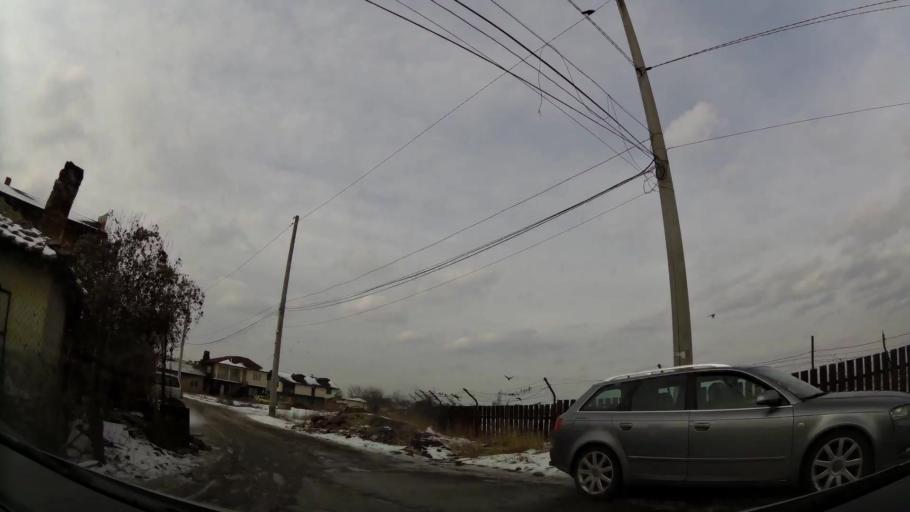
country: BG
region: Sofia-Capital
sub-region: Stolichna Obshtina
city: Sofia
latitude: 42.6934
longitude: 23.3858
